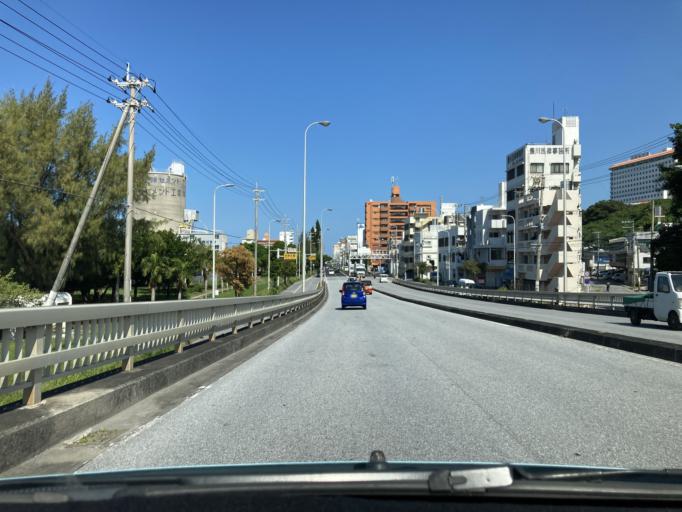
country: JP
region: Okinawa
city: Naha-shi
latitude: 26.2310
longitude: 127.6816
